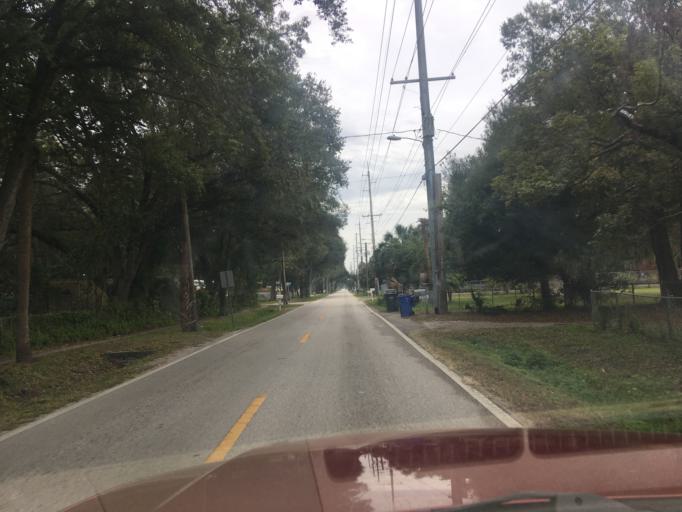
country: US
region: Florida
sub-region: Hillsborough County
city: Gibsonton
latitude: 27.8461
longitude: -82.3737
